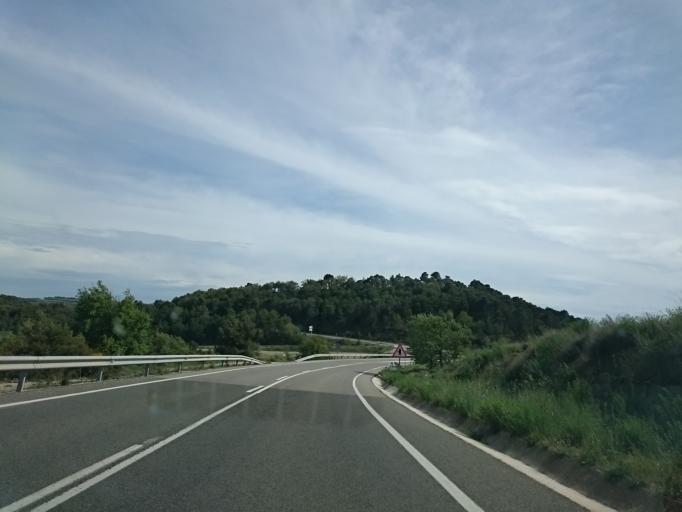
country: ES
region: Catalonia
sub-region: Provincia de Tarragona
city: Santa Coloma de Queralt
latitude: 41.5561
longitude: 1.4050
